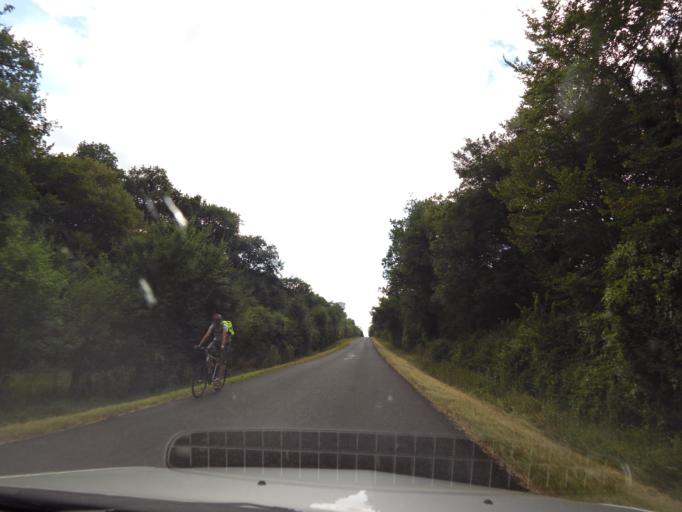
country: FR
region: Poitou-Charentes
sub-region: Departement des Deux-Sevres
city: Beauvoir-sur-Niort
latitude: 46.1483
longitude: -0.4193
